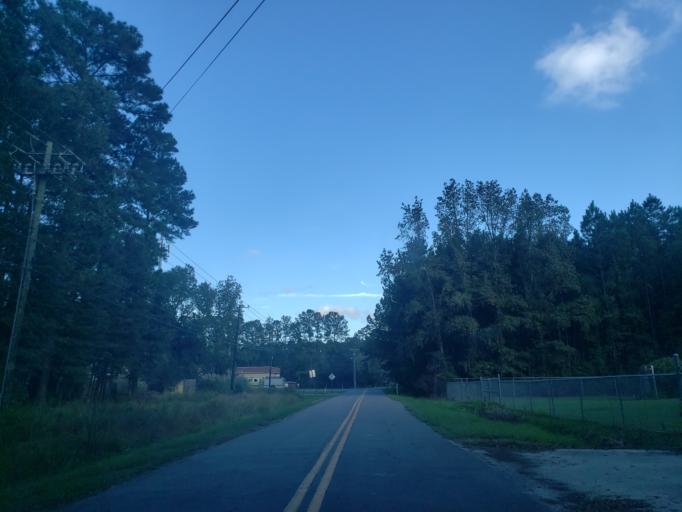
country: US
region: Georgia
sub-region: Chatham County
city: Georgetown
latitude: 31.9948
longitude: -81.2397
